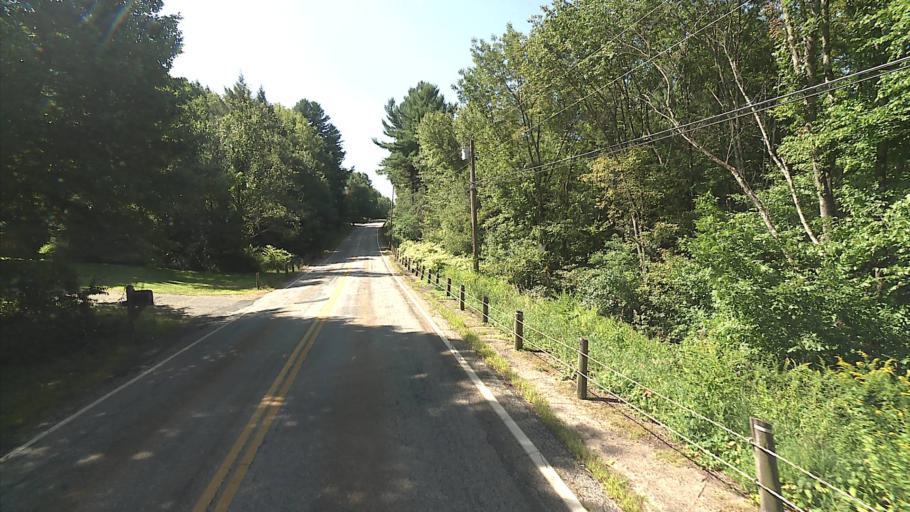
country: US
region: Connecticut
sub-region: Litchfield County
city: Plymouth
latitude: 41.7015
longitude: -73.0554
